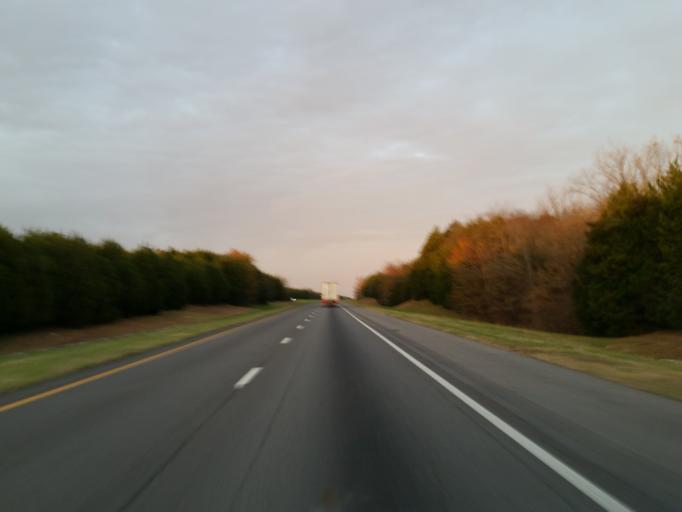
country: US
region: Alabama
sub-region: Sumter County
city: Livingston
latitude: 32.6476
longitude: -88.1936
